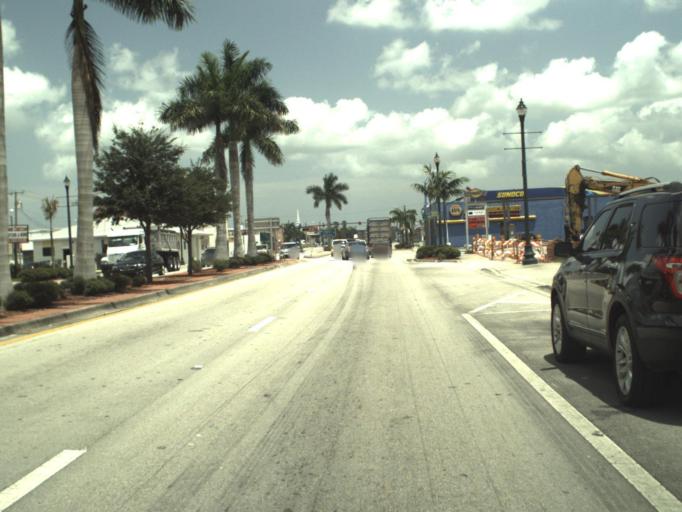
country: US
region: Florida
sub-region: Palm Beach County
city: Belle Glade
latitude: 26.6834
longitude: -80.6677
